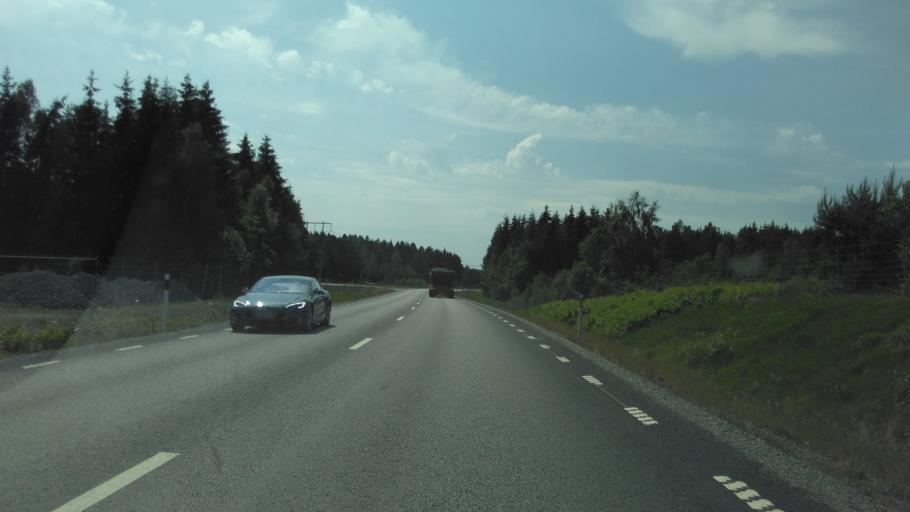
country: SE
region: Vaestra Goetaland
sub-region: Lidkopings Kommun
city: Lidkoping
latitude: 58.4495
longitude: 12.9792
